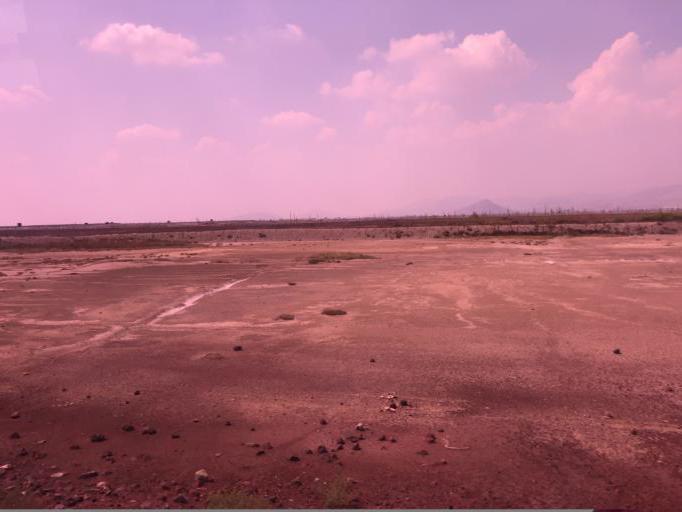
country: MX
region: Mexico
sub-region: Atenco
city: Colonia el Salado
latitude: 19.5470
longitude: -98.9849
